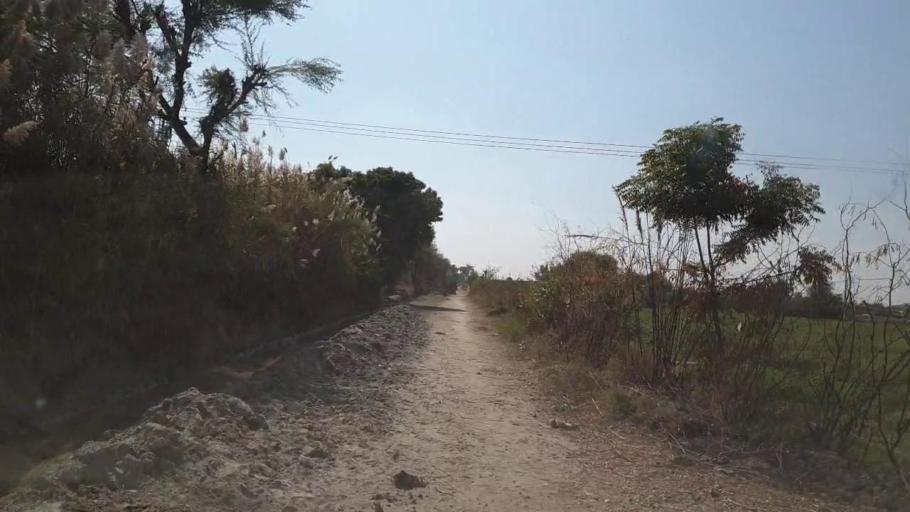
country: PK
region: Sindh
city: Mirpur Khas
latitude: 25.7365
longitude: 69.0990
